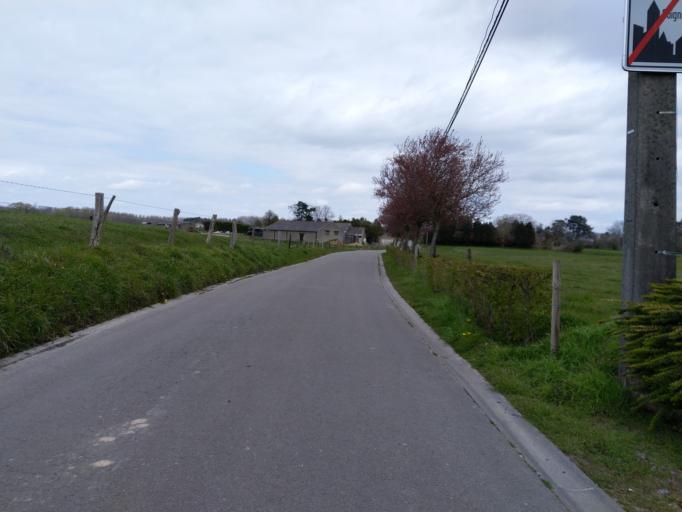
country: BE
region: Wallonia
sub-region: Province du Hainaut
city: Mons
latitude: 50.5184
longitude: 4.0045
